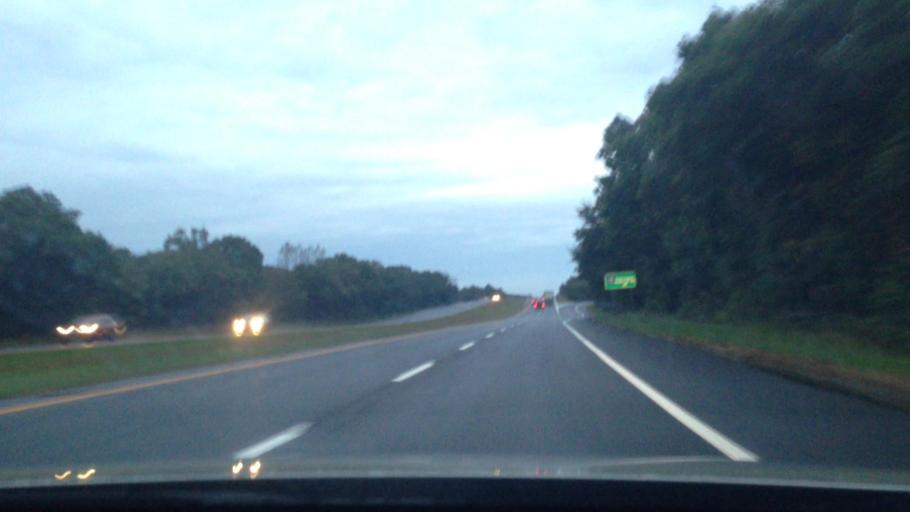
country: US
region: New York
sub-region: Suffolk County
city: Holtsville
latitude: 40.7865
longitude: -73.0513
